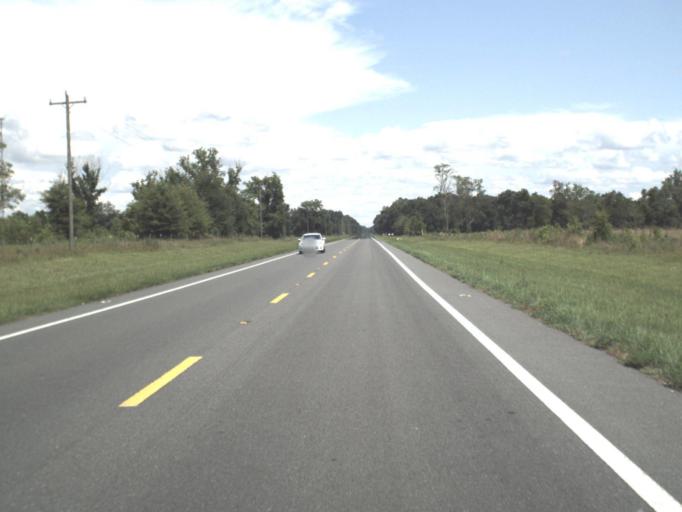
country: US
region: Florida
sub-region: Lafayette County
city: Mayo
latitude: 30.0755
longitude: -83.2091
